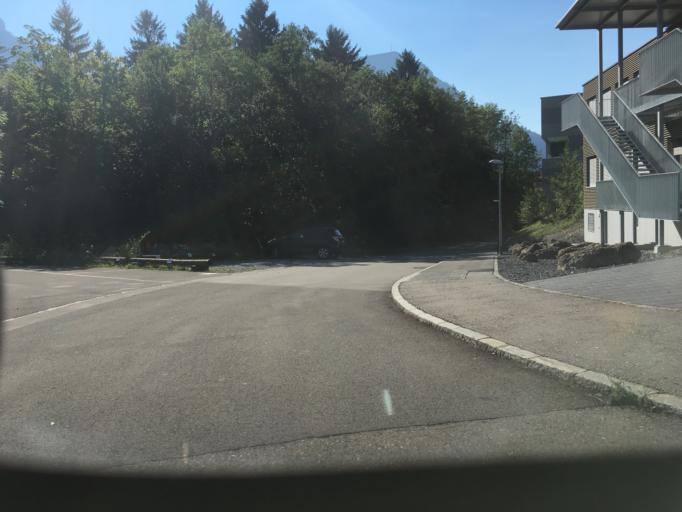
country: CH
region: Schwyz
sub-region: Bezirk Schwyz
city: Goldau
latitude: 47.0455
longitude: 8.5531
